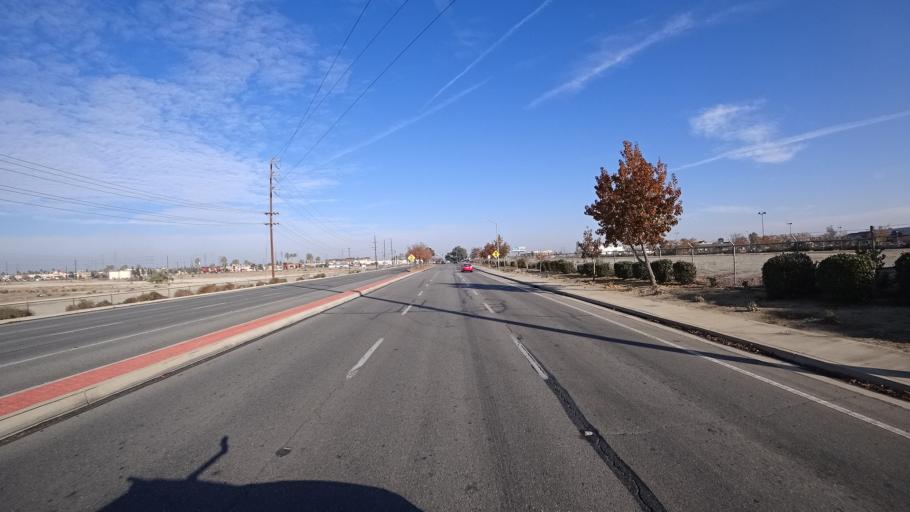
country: US
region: California
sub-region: Kern County
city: Greenacres
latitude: 35.3809
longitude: -119.0922
